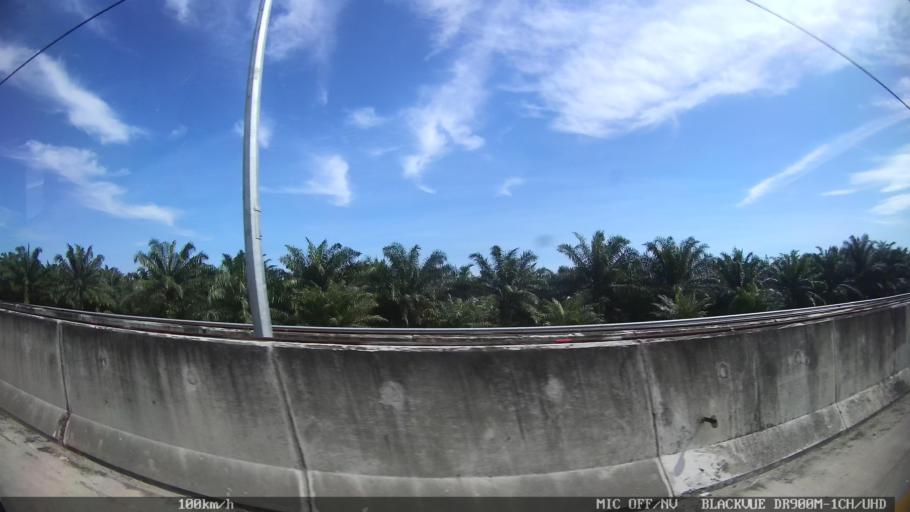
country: ID
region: North Sumatra
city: Sunggal
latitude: 3.6385
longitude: 98.6101
